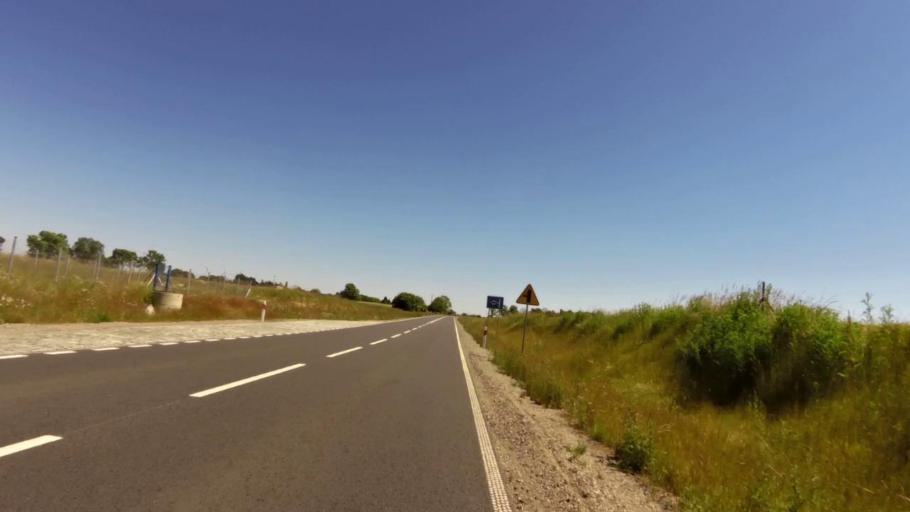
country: PL
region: West Pomeranian Voivodeship
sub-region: Powiat kolobrzeski
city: Goscino
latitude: 54.0432
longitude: 15.6543
